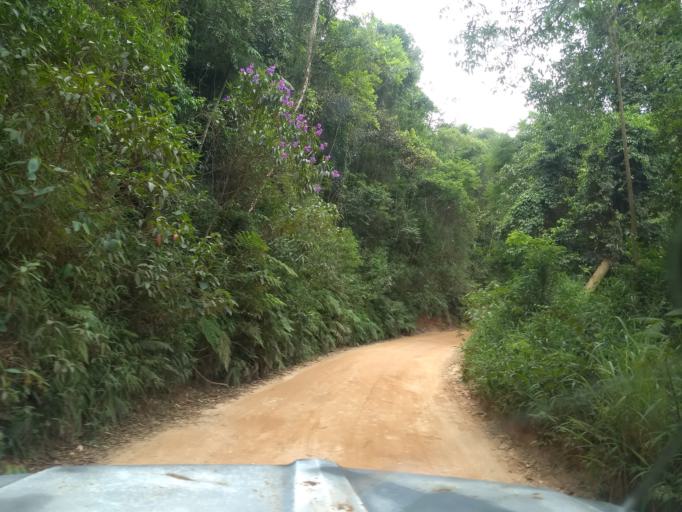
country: BR
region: Sao Paulo
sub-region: Cabreuva
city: Cabreuva
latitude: -23.4090
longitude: -47.2001
